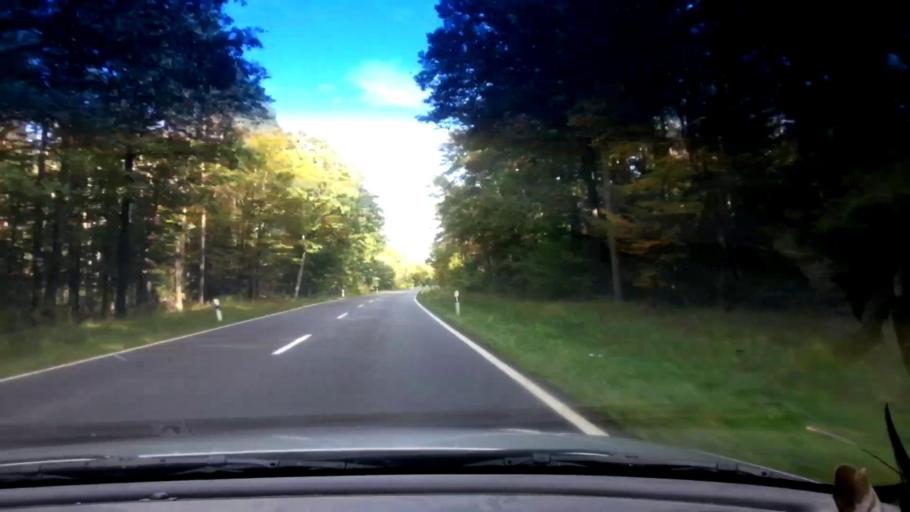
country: DE
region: Bavaria
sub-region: Upper Franconia
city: Strullendorf
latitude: 49.8594
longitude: 10.9637
